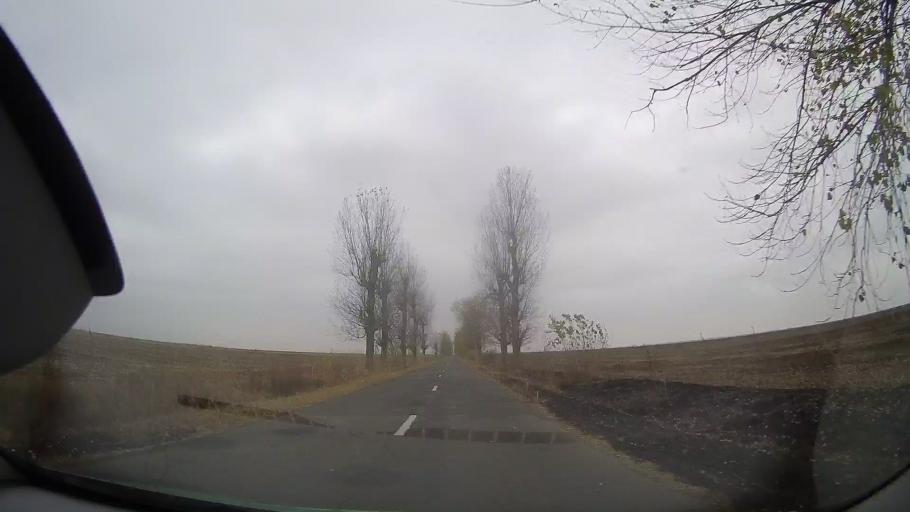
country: RO
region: Ialomita
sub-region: Comuna Grindu
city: Grindu
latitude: 44.7710
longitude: 26.8849
